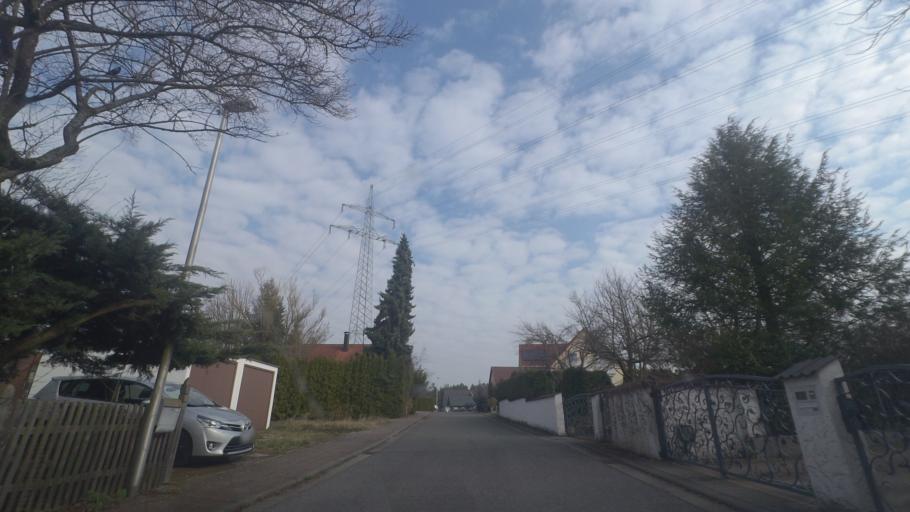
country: DE
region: Bavaria
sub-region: Regierungsbezirk Mittelfranken
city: Winkelhaid
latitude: 49.4121
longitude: 11.2983
